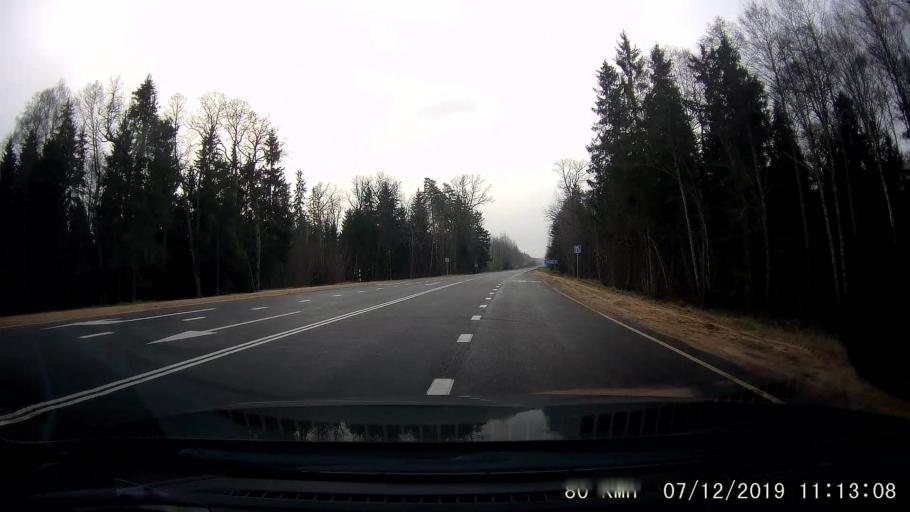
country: BY
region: Grodnenskaya
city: Iwye
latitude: 53.8788
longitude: 25.7396
